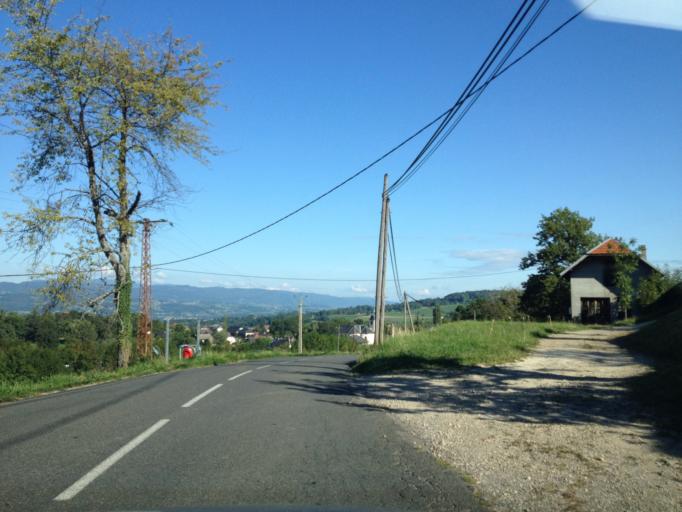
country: FR
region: Rhone-Alpes
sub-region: Departement de la Haute-Savoie
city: Cusy
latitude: 45.7312
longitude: 6.0050
